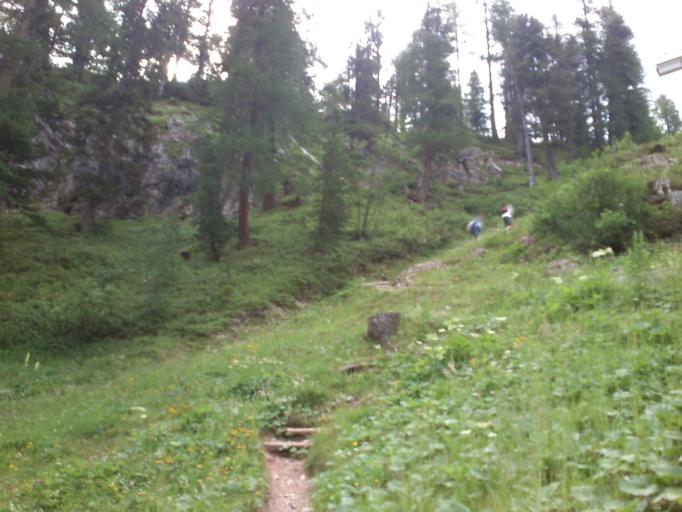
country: IT
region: Veneto
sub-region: Provincia di Belluno
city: Selva di Cadore
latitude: 46.5166
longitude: 12.0400
